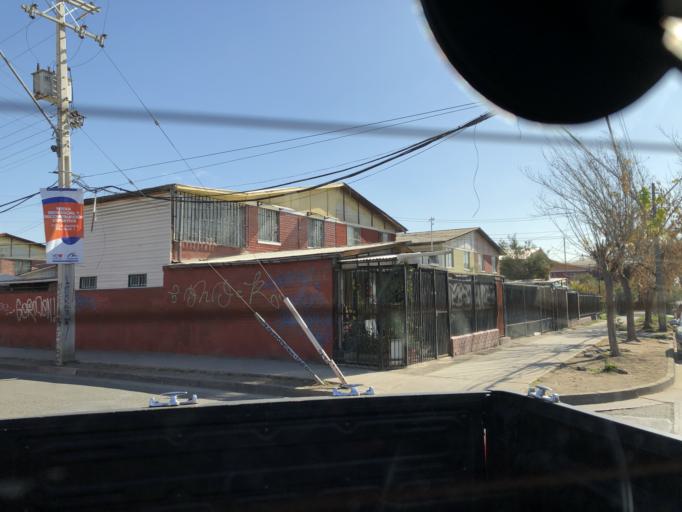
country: CL
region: Santiago Metropolitan
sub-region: Provincia de Cordillera
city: Puente Alto
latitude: -33.5654
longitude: -70.5795
